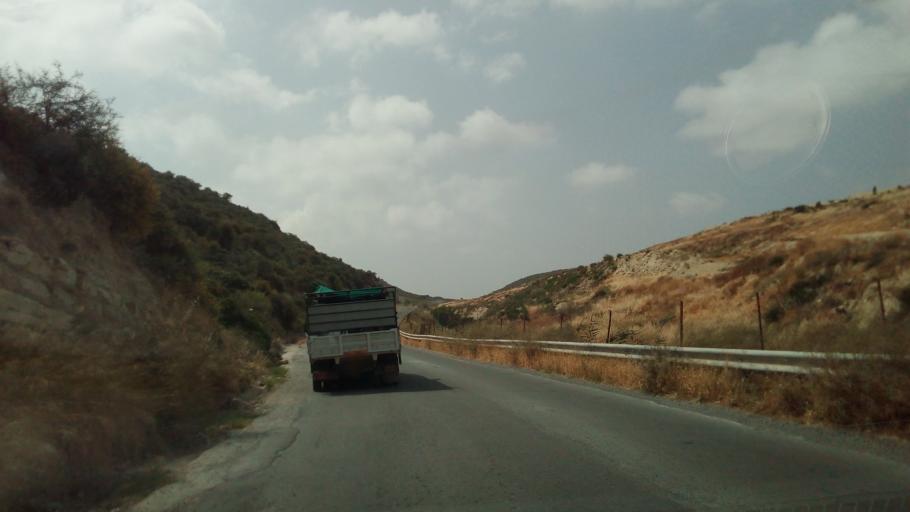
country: CY
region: Limassol
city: Pano Polemidia
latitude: 34.7514
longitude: 32.9537
